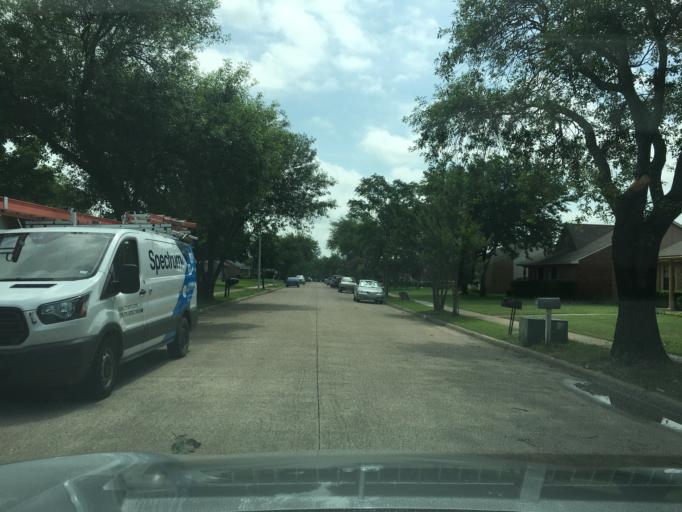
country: US
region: Texas
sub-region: Dallas County
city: Garland
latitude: 32.9225
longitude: -96.6715
